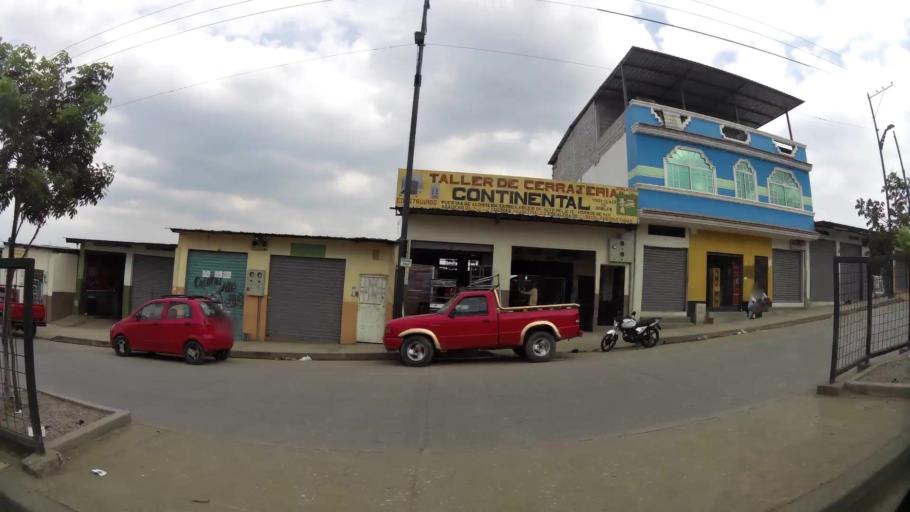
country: EC
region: Guayas
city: Santa Lucia
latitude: -2.1055
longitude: -79.9566
